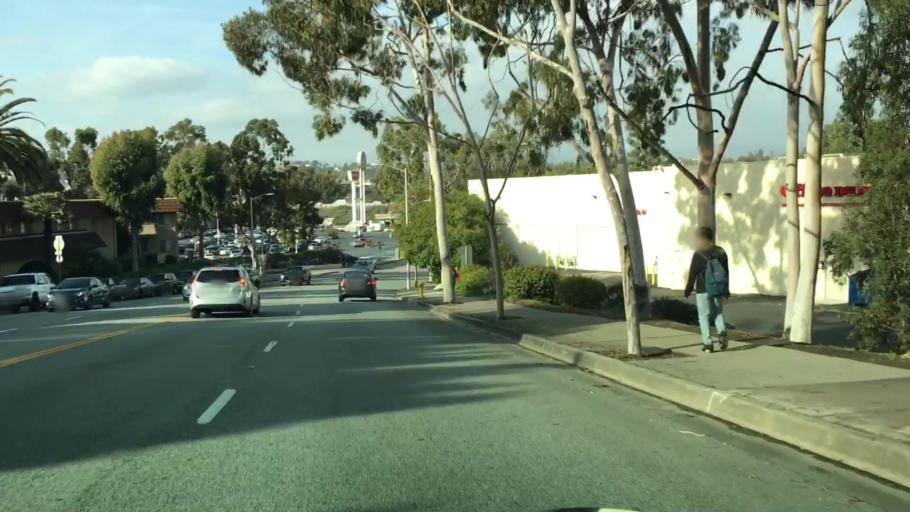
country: US
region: California
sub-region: Los Angeles County
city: Montebello
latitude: 34.0301
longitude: -118.1248
